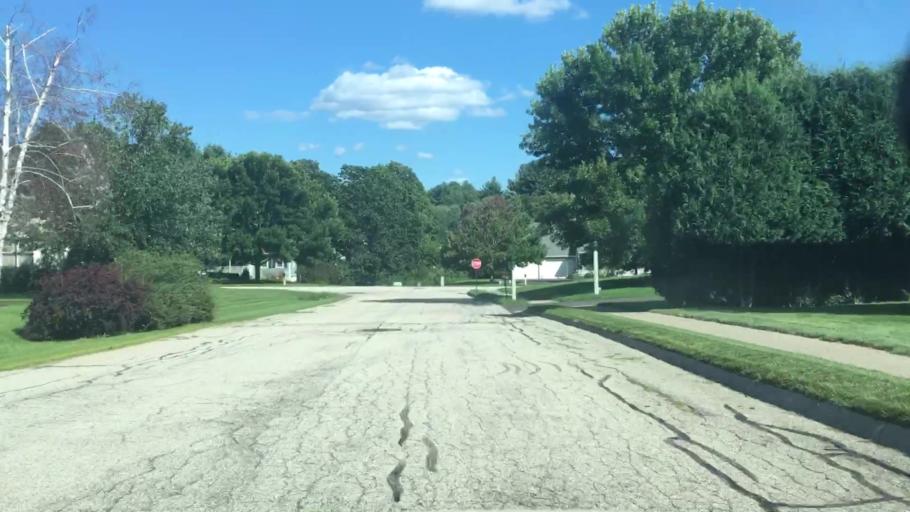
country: US
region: New Hampshire
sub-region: Strafford County
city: Dover
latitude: 43.1675
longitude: -70.8866
